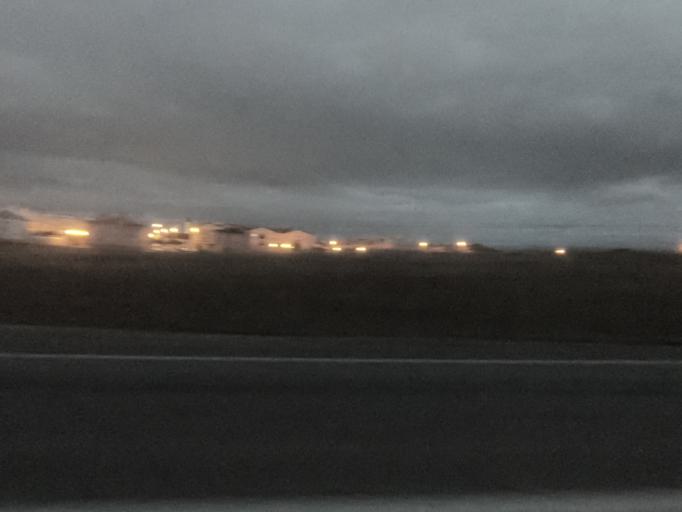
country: PT
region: Setubal
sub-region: Barreiro
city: Santo Antonio da Charneca
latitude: 38.6252
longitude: -9.0362
